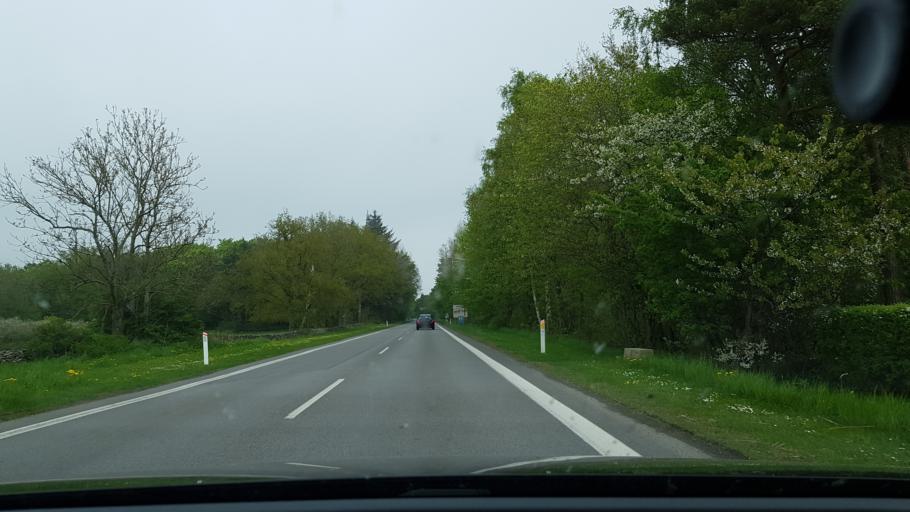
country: DK
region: Capital Region
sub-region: Bornholm Kommune
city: Nexo
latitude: 55.0489
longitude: 15.1158
